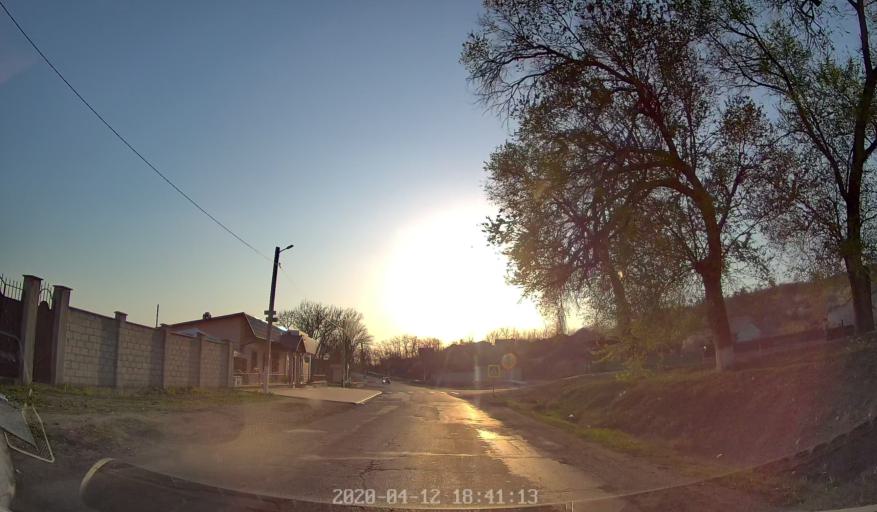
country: MD
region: Chisinau
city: Ciorescu
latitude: 47.1358
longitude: 28.9552
